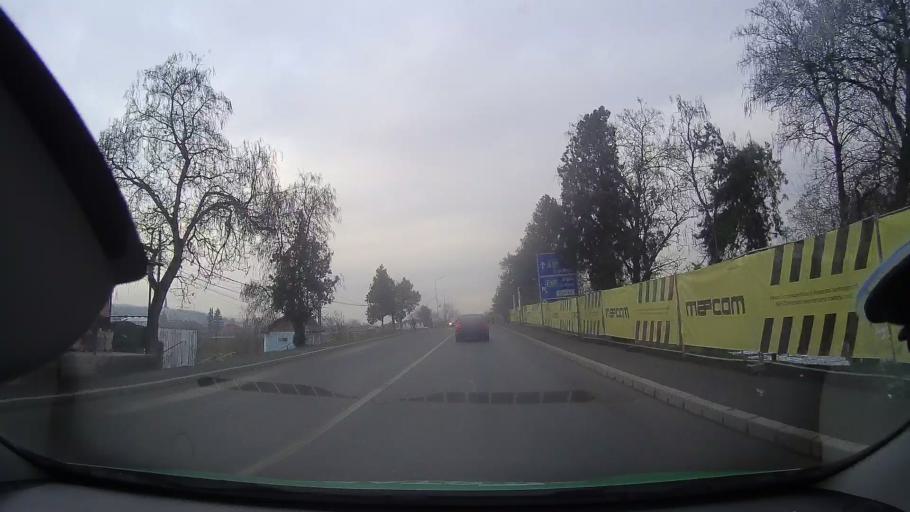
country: RO
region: Mures
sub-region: Comuna Ludus
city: Ludus
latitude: 46.4788
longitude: 24.0958
